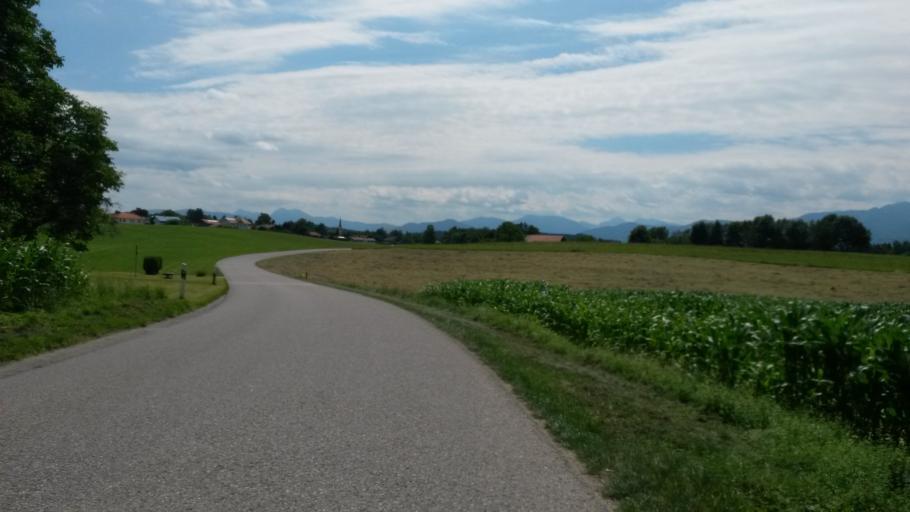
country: DE
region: Bavaria
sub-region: Upper Bavaria
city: Chieming
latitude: 47.8999
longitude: 12.5281
